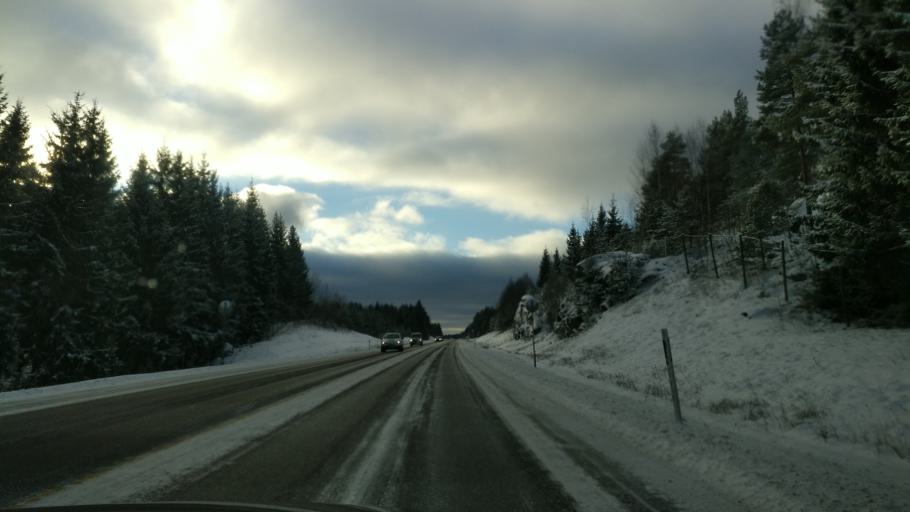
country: FI
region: Paijanne Tavastia
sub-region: Lahti
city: Heinola
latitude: 61.3496
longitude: 26.2148
